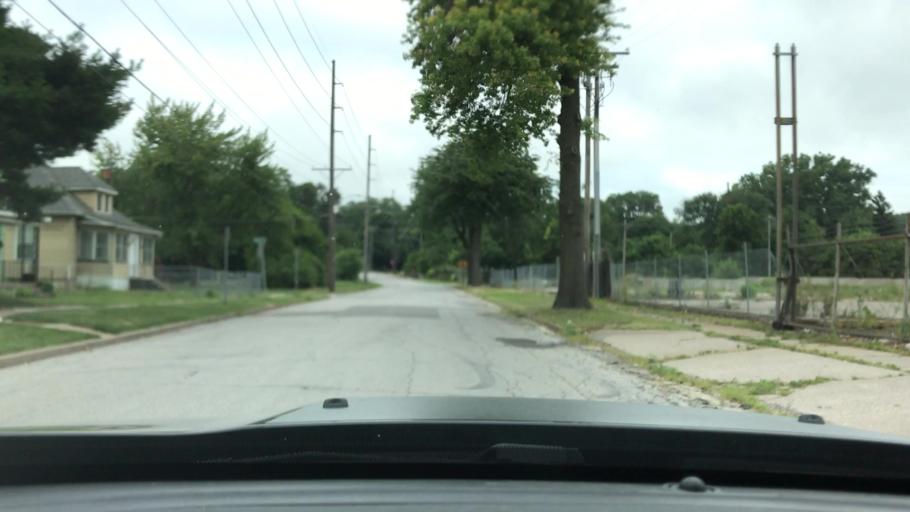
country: US
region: Illinois
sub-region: Rock Island County
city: Rock Island
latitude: 41.5155
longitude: -90.6212
